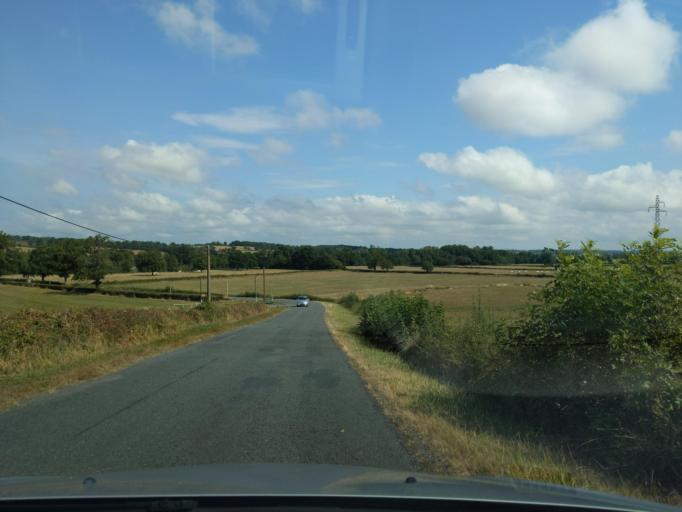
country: FR
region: Bourgogne
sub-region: Departement de Saone-et-Loire
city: Bourbon-Lancy
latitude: 46.6443
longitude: 3.7741
